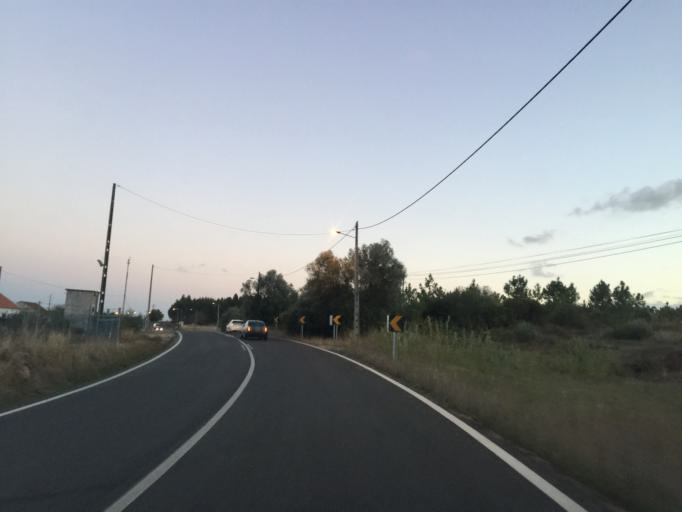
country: PT
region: Lisbon
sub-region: Alenquer
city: Alenquer
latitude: 39.1306
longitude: -8.9952
